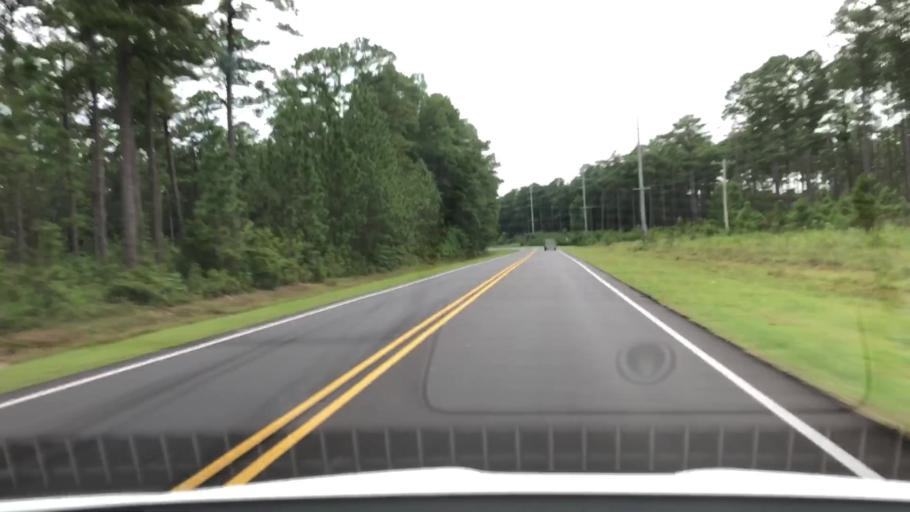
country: US
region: North Carolina
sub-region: Jones County
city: Maysville
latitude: 34.8194
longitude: -77.1473
